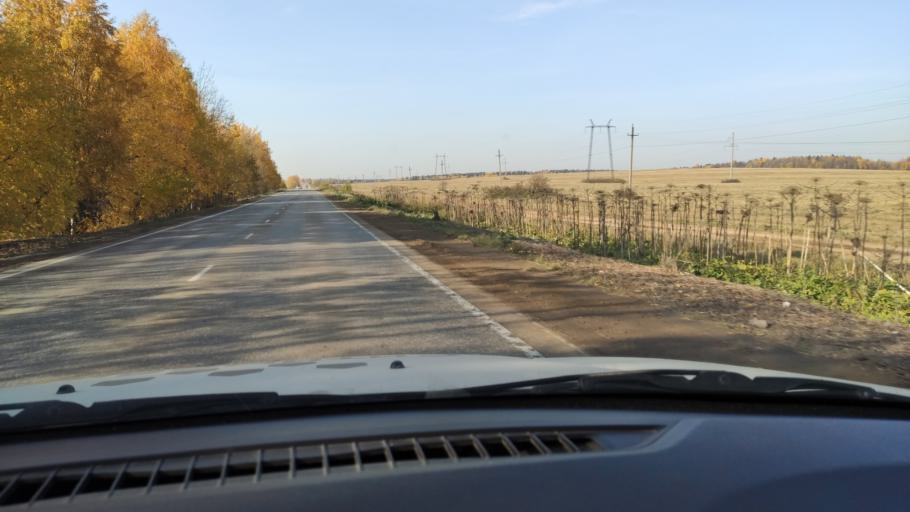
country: RU
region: Perm
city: Sylva
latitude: 58.0294
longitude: 56.6996
